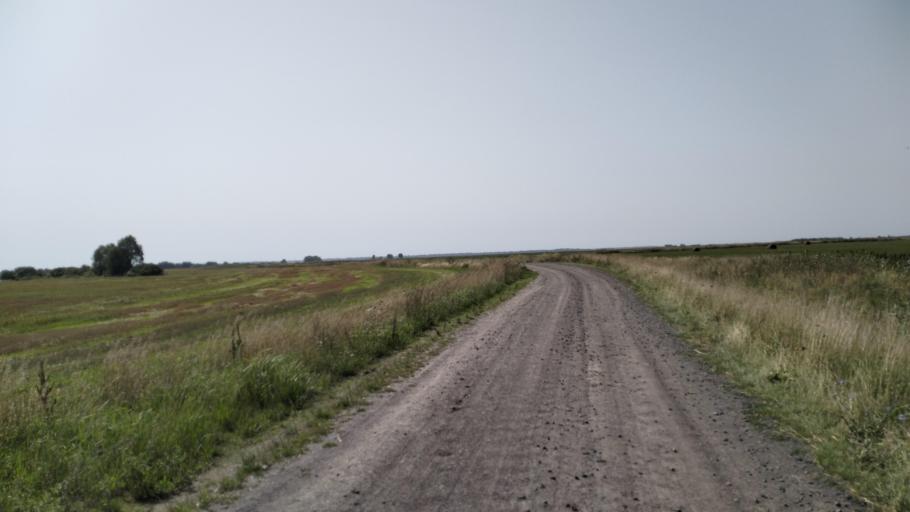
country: BY
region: Brest
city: Davyd-Haradok
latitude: 52.0112
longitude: 27.1660
